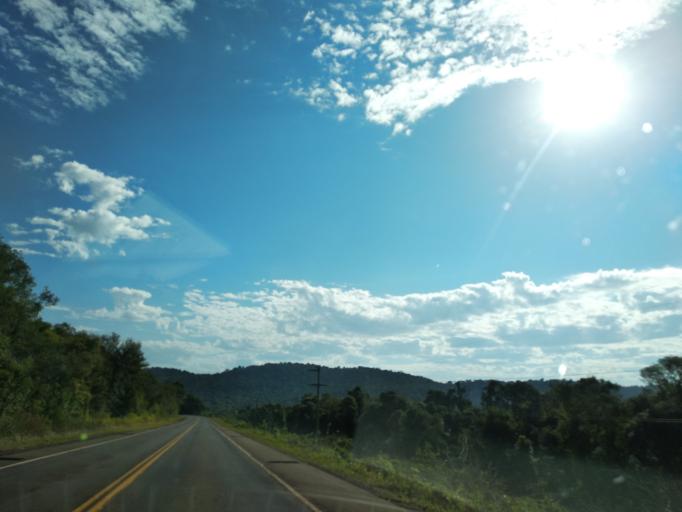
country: AR
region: Misiones
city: Aristobulo del Valle
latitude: -27.0921
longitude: -54.9457
